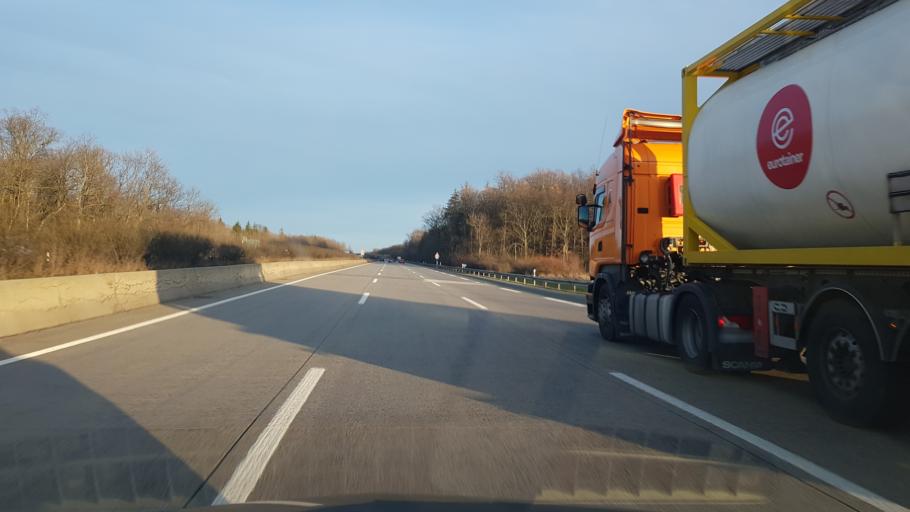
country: DE
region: Thuringia
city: Rockhausen
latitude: 50.9110
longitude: 11.0762
